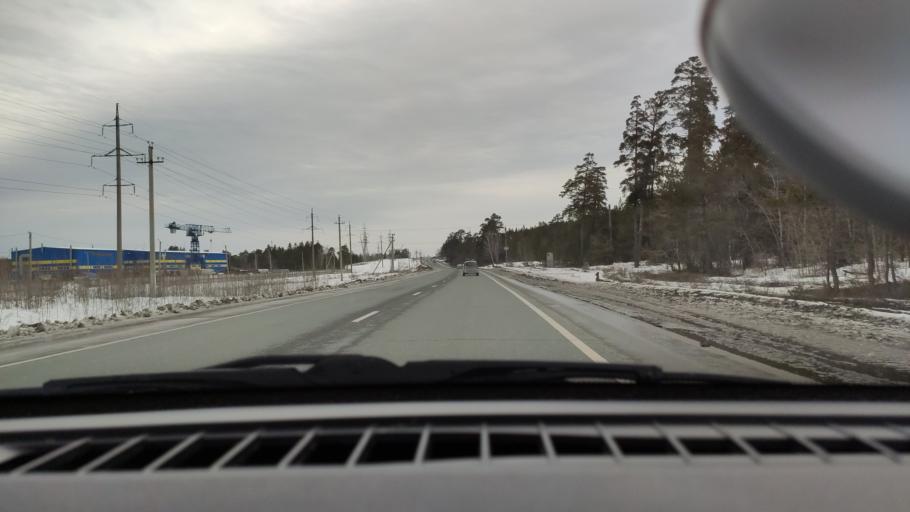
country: RU
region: Samara
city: Kurumoch
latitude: 53.4718
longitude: 50.0653
